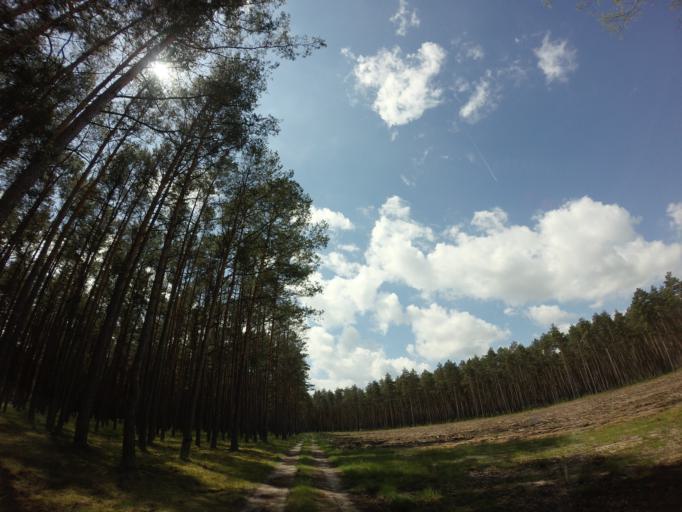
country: PL
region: West Pomeranian Voivodeship
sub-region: Powiat drawski
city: Kalisz Pomorski
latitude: 53.1861
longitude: 15.9410
